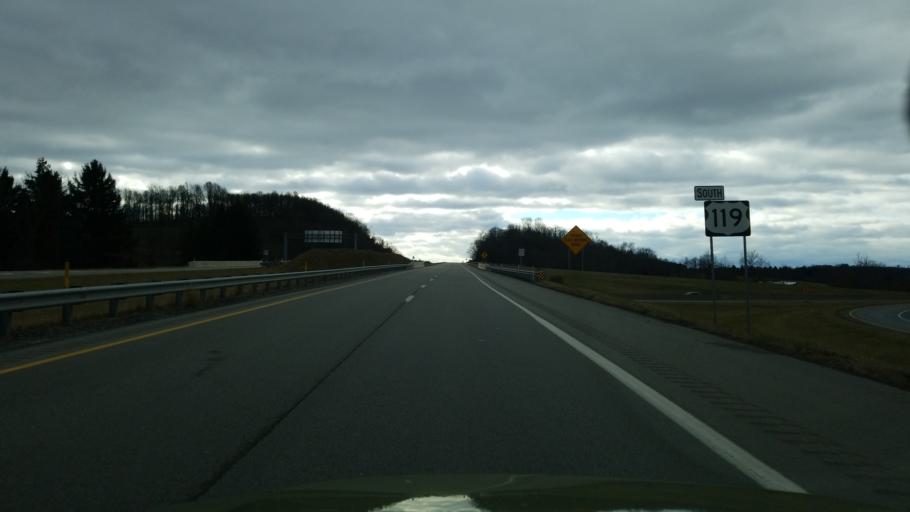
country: US
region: Pennsylvania
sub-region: Indiana County
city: Chevy Chase Heights
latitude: 40.6689
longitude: -79.1133
